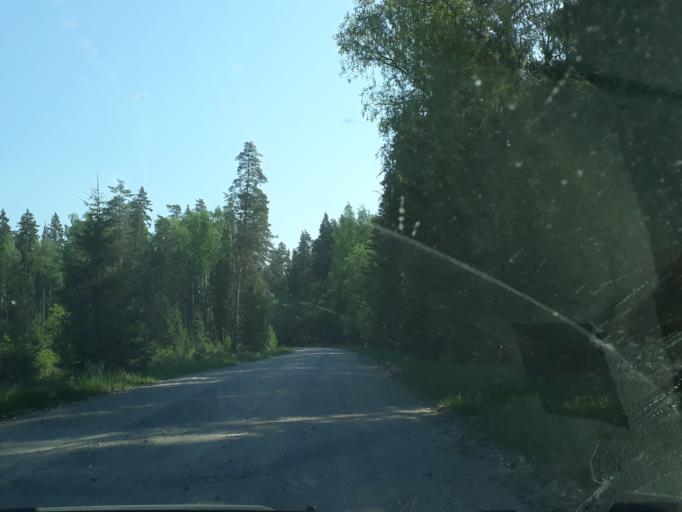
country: LV
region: Ligatne
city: Ligatne
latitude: 57.2782
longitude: 25.0742
